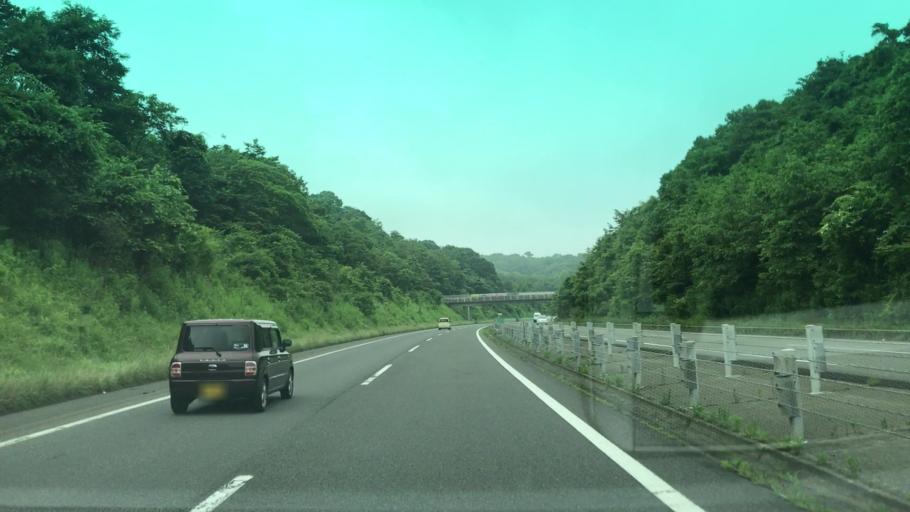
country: JP
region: Hokkaido
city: Shiraoi
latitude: 42.4800
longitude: 141.2206
